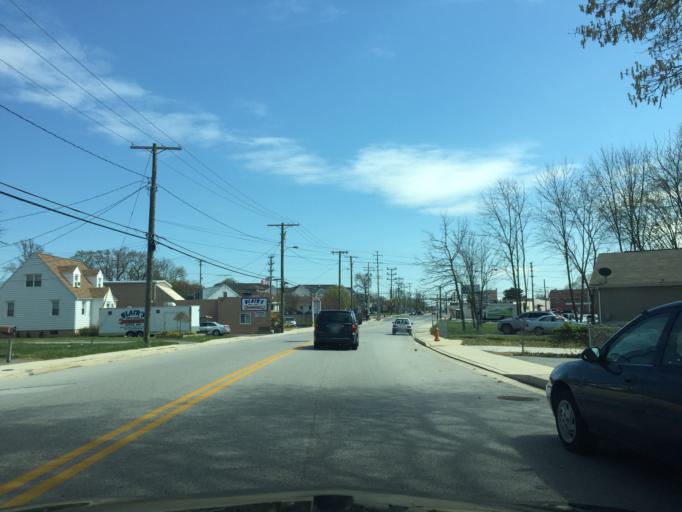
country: US
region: Maryland
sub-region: Baltimore County
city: Middle River
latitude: 39.3168
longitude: -76.4520
